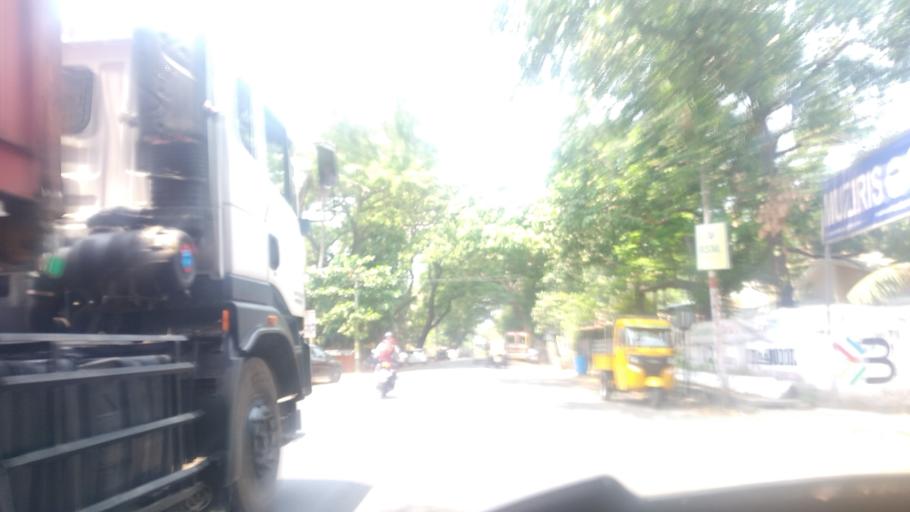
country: IN
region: Kerala
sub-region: Thrissur District
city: Kodungallur
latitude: 10.2447
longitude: 76.1901
